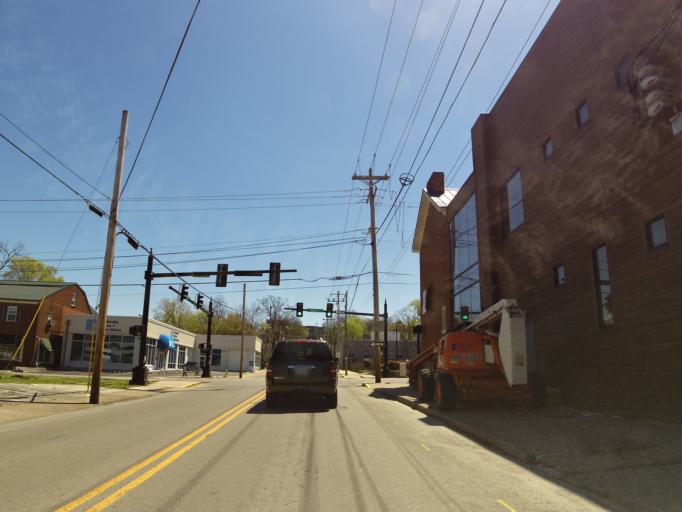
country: US
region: Kentucky
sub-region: Warren County
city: Bowling Green
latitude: 36.9940
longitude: -86.4396
